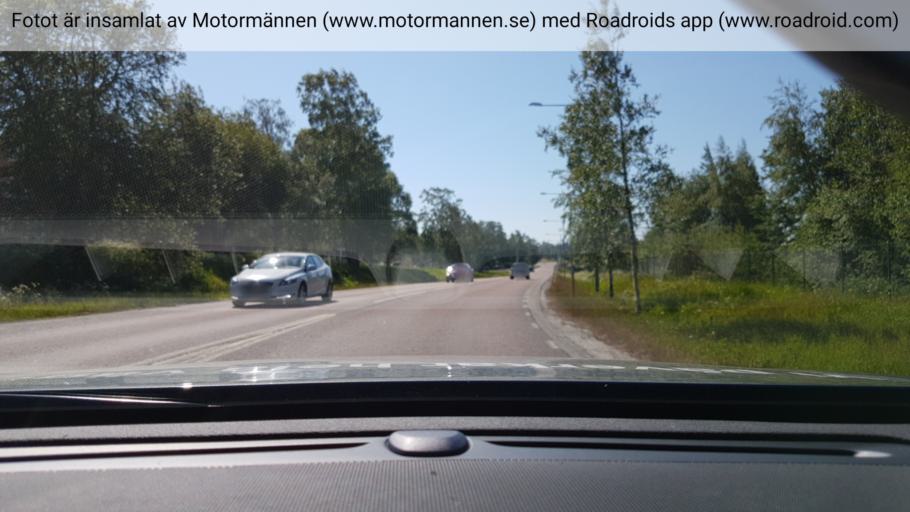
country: SE
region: Vaesterbotten
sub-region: Umea Kommun
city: Holmsund
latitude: 63.7117
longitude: 20.3593
